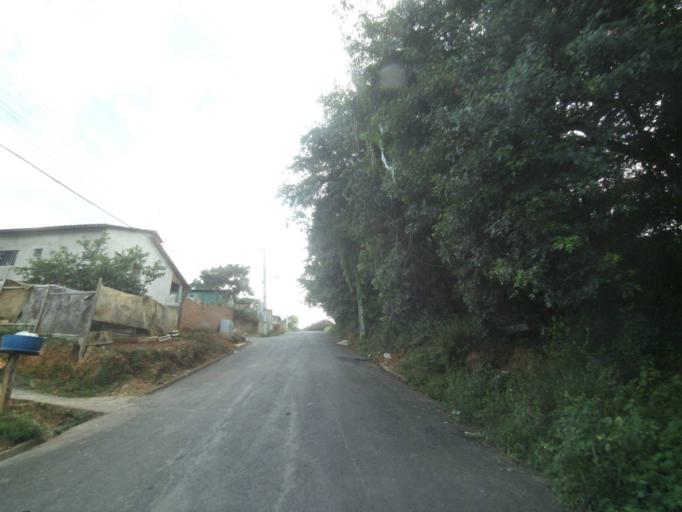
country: BR
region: Parana
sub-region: Telemaco Borba
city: Telemaco Borba
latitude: -24.3257
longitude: -50.6081
